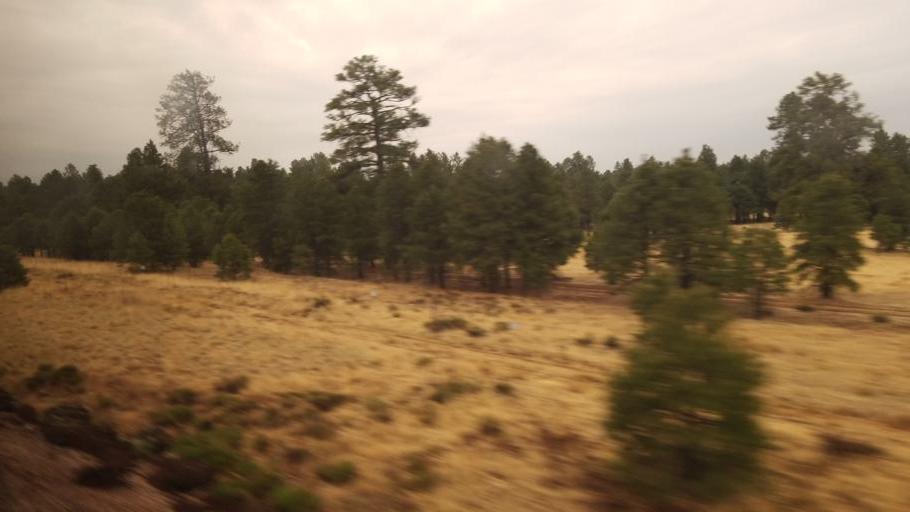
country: US
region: Arizona
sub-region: Coconino County
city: Parks
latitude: 35.2432
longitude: -111.8729
